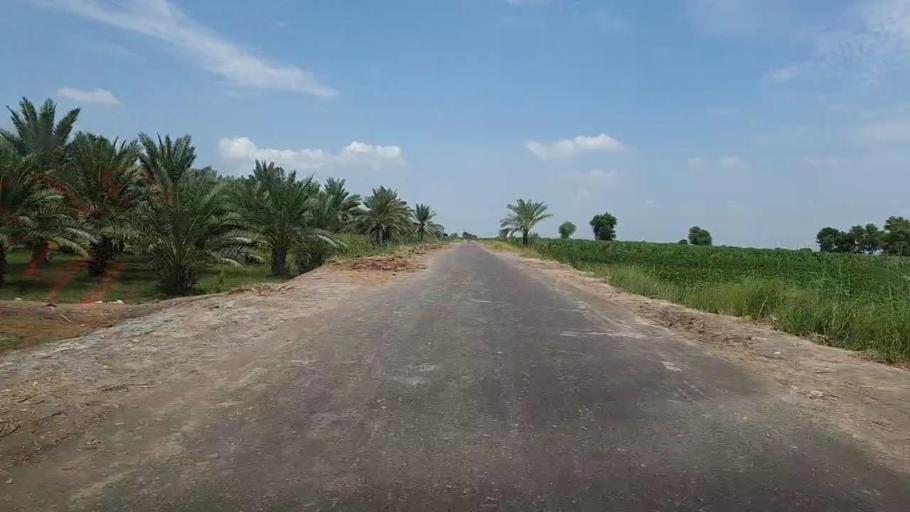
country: PK
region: Sindh
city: Bhiria
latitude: 26.9331
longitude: 68.2152
